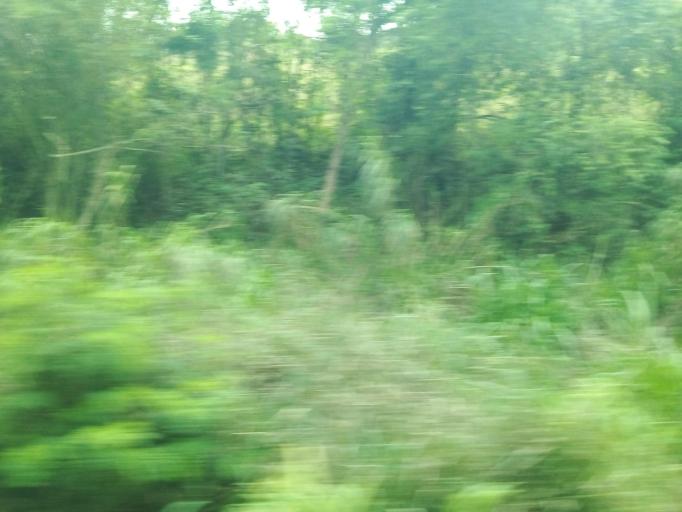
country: BR
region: Minas Gerais
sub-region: Nova Era
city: Nova Era
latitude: -19.7777
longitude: -43.0696
